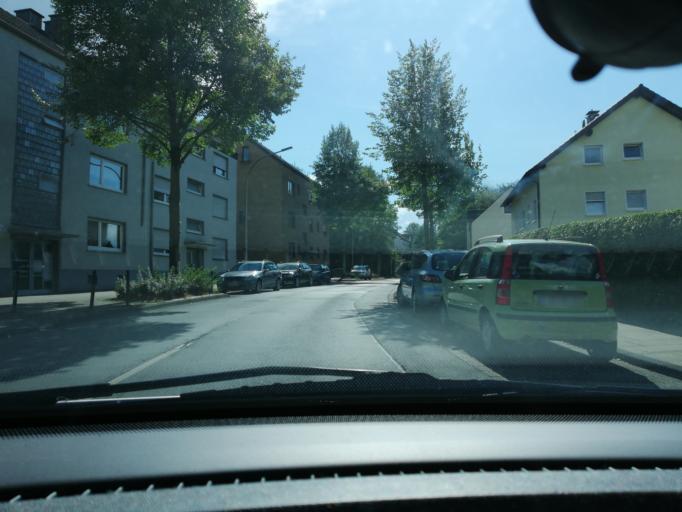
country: DE
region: North Rhine-Westphalia
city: Witten
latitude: 51.4512
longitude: 7.4016
